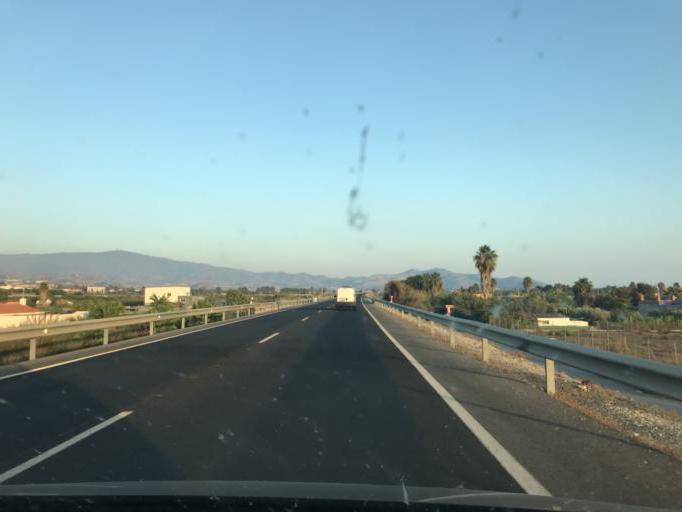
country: ES
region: Andalusia
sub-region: Provincia de Granada
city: El Varadero
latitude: 36.7387
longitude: -3.5378
